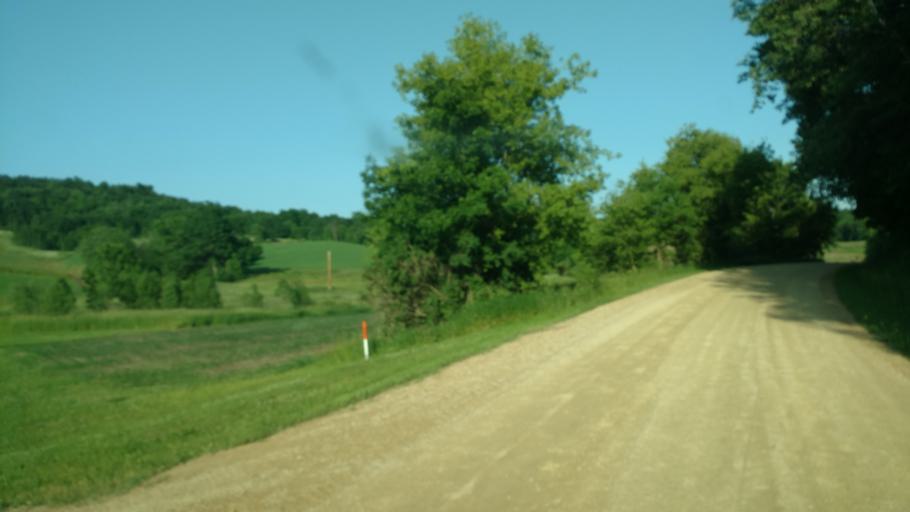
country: US
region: Wisconsin
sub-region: Vernon County
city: Hillsboro
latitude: 43.6303
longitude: -90.3431
